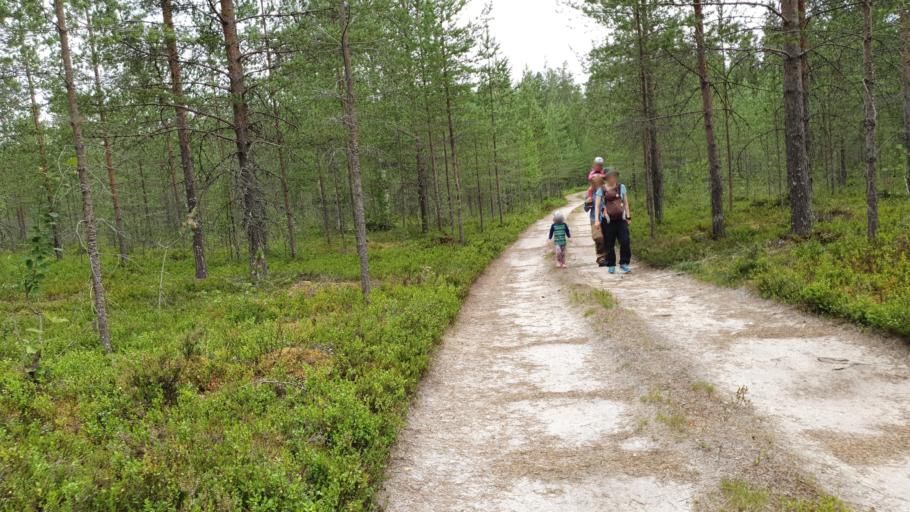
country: FI
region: Kainuu
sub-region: Kehys-Kainuu
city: Kuhmo
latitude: 64.7311
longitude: 29.7172
